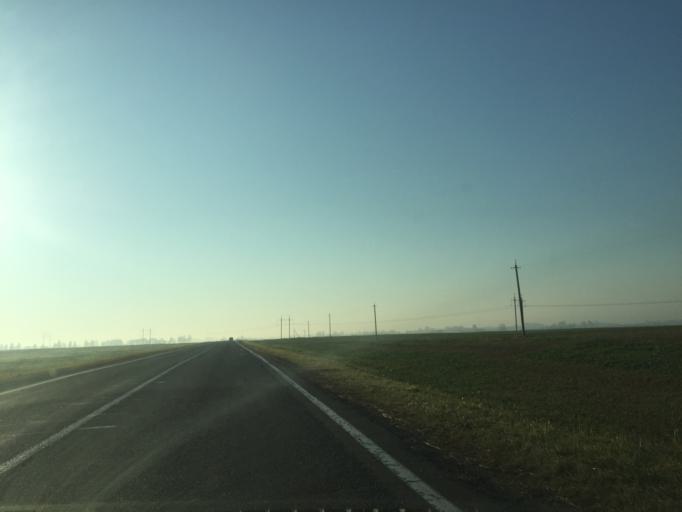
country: BY
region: Gomel
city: Buda-Kashalyova
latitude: 52.8298
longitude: 30.7137
